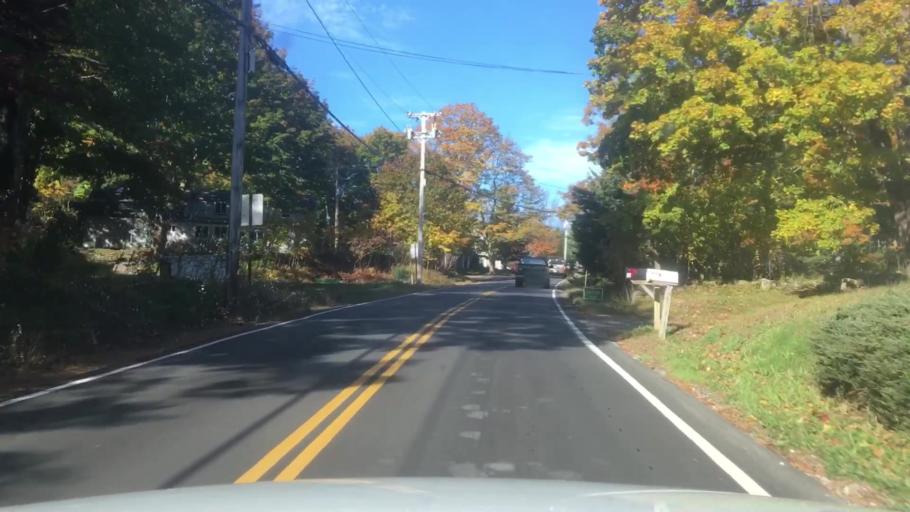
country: US
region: Maine
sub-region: Sagadahoc County
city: Phippsburg
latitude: 43.8038
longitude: -69.7546
